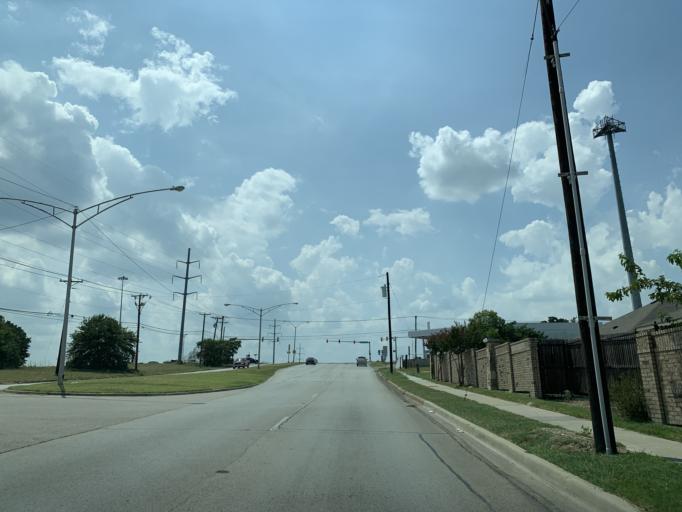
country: US
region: Texas
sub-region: Tarrant County
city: Richland Hills
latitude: 32.7664
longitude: -97.2106
